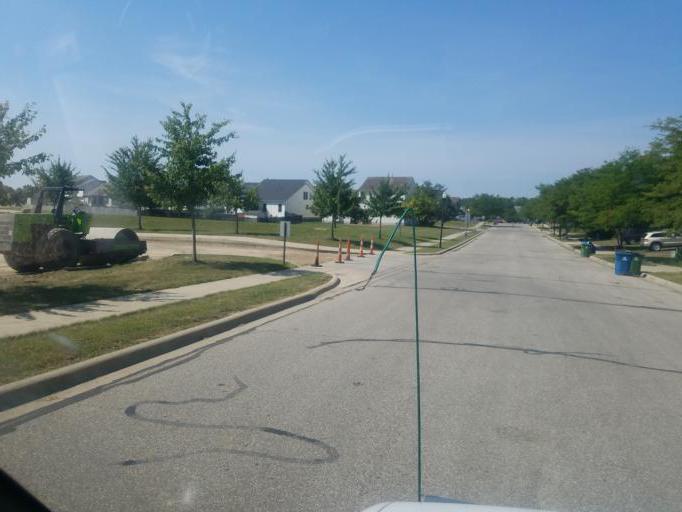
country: US
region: Ohio
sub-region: Union County
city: Marysville
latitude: 40.2649
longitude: -83.3856
